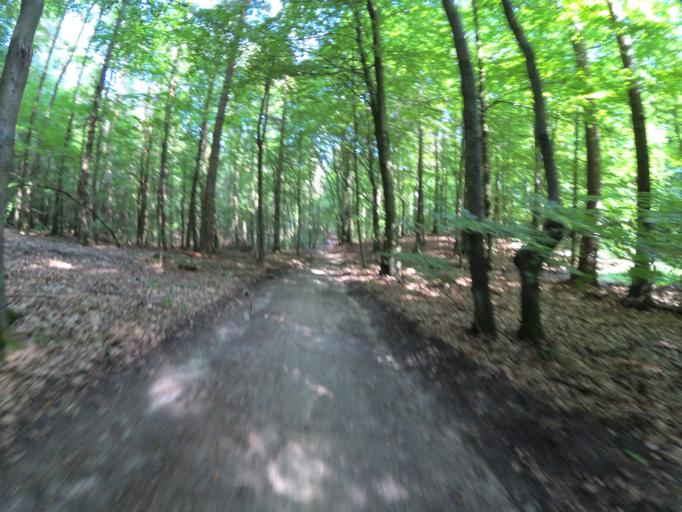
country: PL
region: Pomeranian Voivodeship
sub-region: Gdynia
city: Wielki Kack
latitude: 54.5013
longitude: 18.4906
